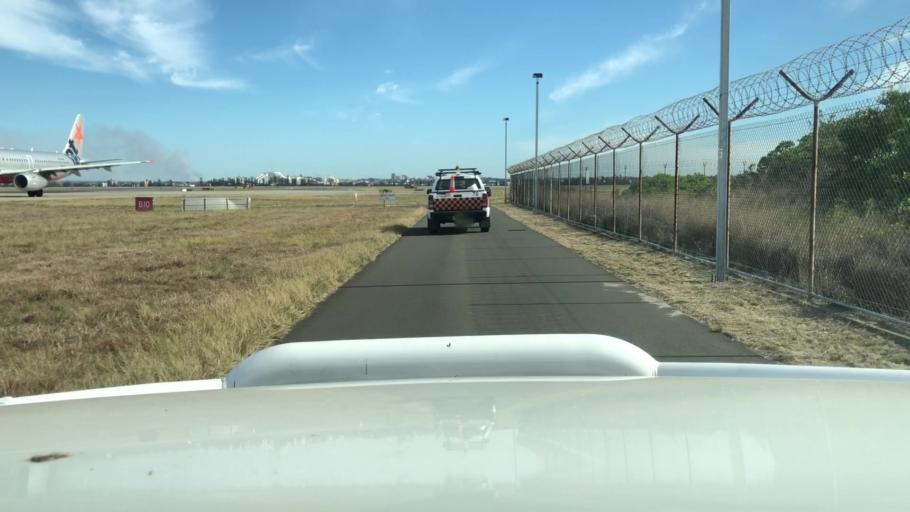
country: AU
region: New South Wales
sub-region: Botany Bay
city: Botany
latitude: -33.9503
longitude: 151.1820
